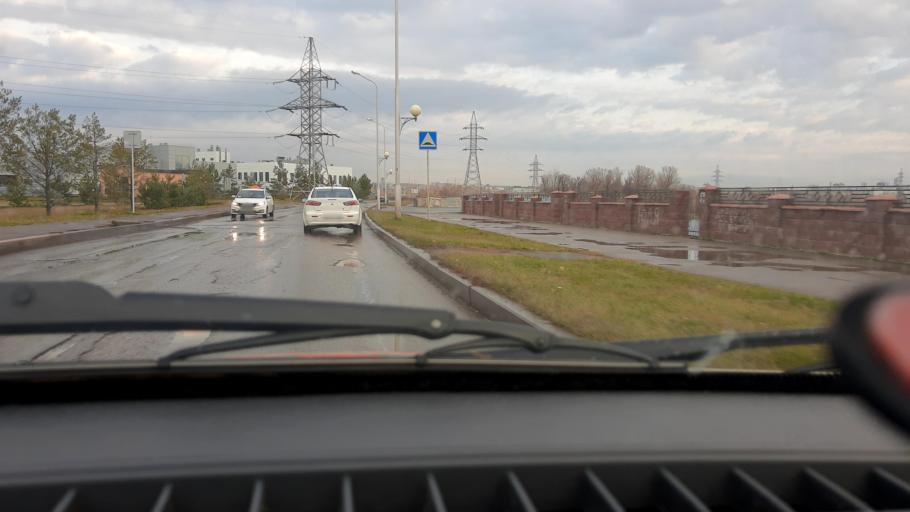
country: RU
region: Bashkortostan
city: Ufa
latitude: 54.7815
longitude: 56.0775
